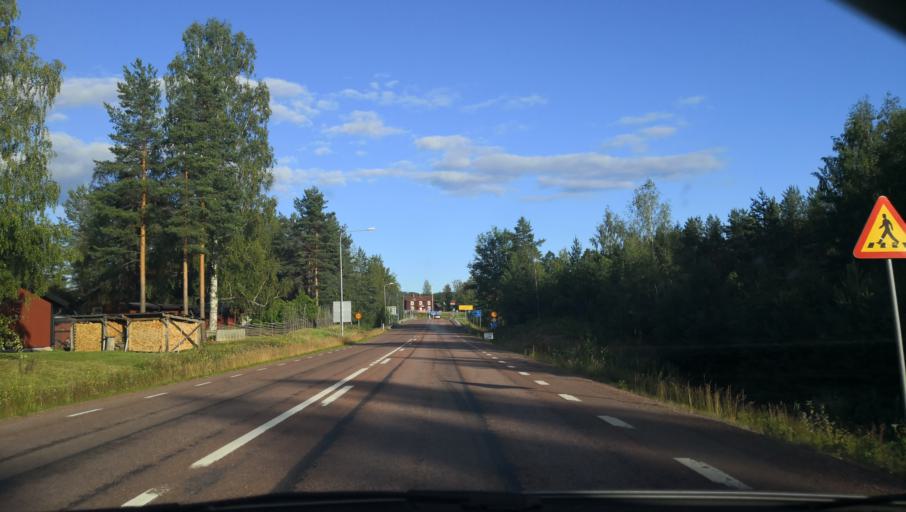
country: SE
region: Dalarna
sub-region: Alvdalens Kommun
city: AElvdalen
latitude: 61.2570
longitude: 14.0284
